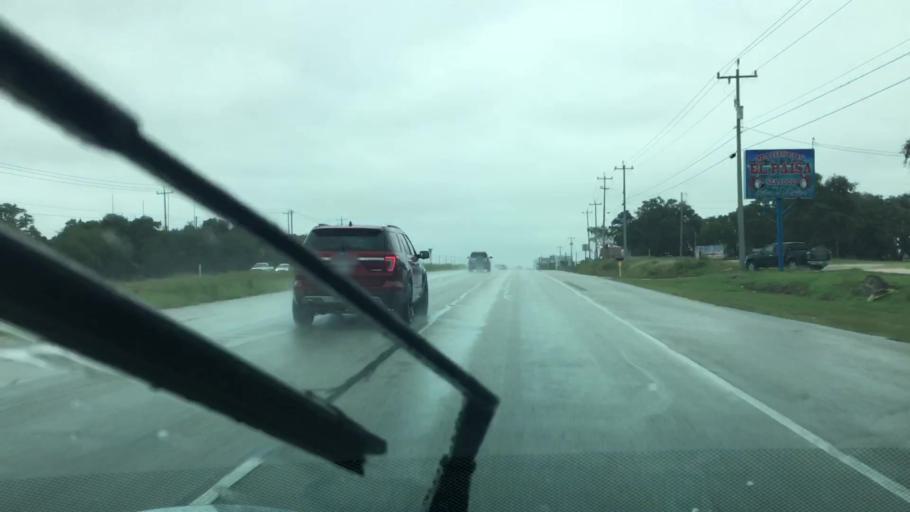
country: US
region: Texas
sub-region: Comal County
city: Bulverde
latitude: 29.7289
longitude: -98.4406
